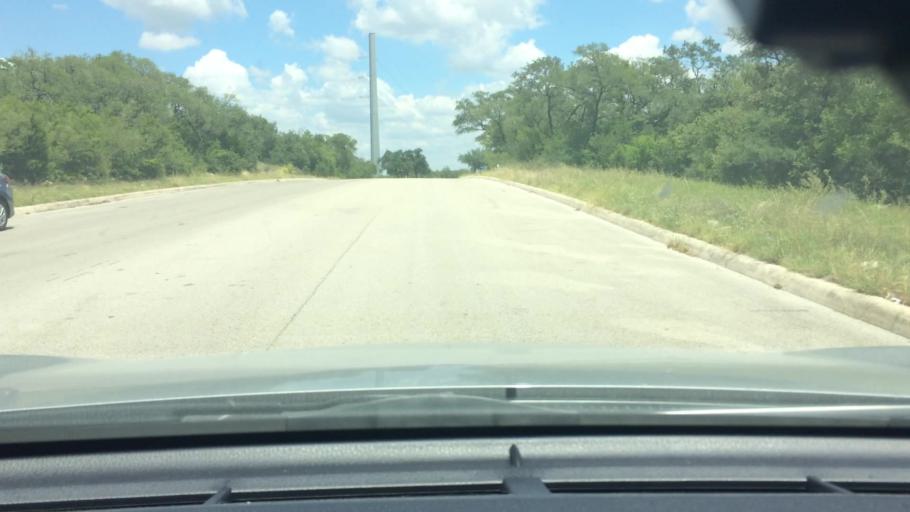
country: US
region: Texas
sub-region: Bexar County
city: Leon Valley
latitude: 29.4724
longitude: -98.6944
